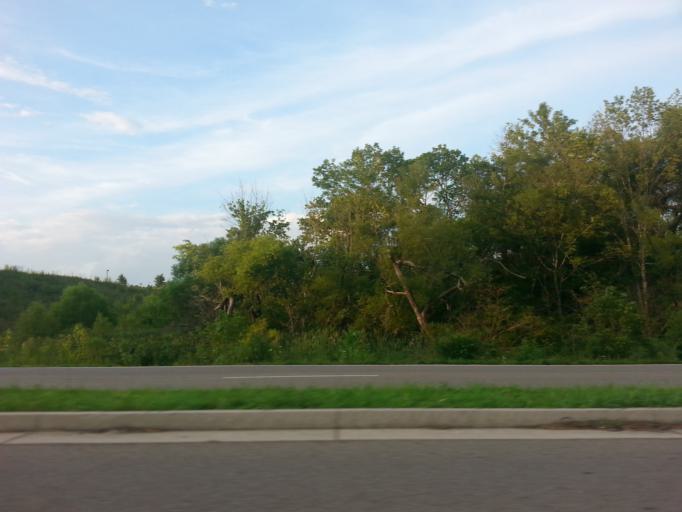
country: US
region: Tennessee
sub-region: Knox County
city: Knoxville
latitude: 36.0847
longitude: -83.9373
